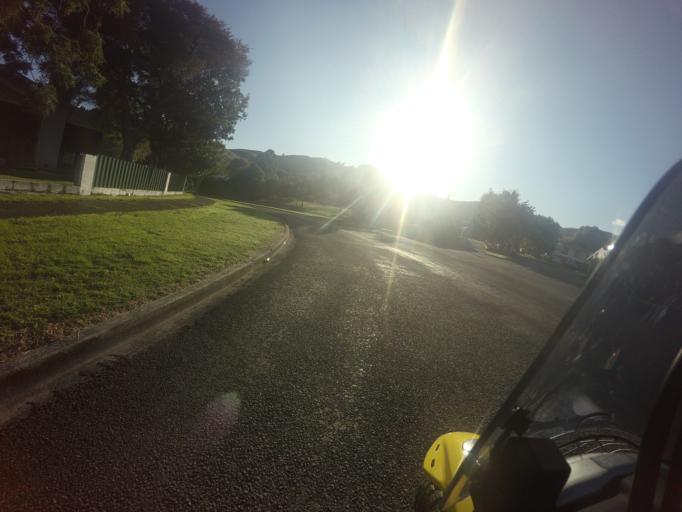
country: NZ
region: Gisborne
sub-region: Gisborne District
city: Gisborne
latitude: -38.6730
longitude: 178.0599
